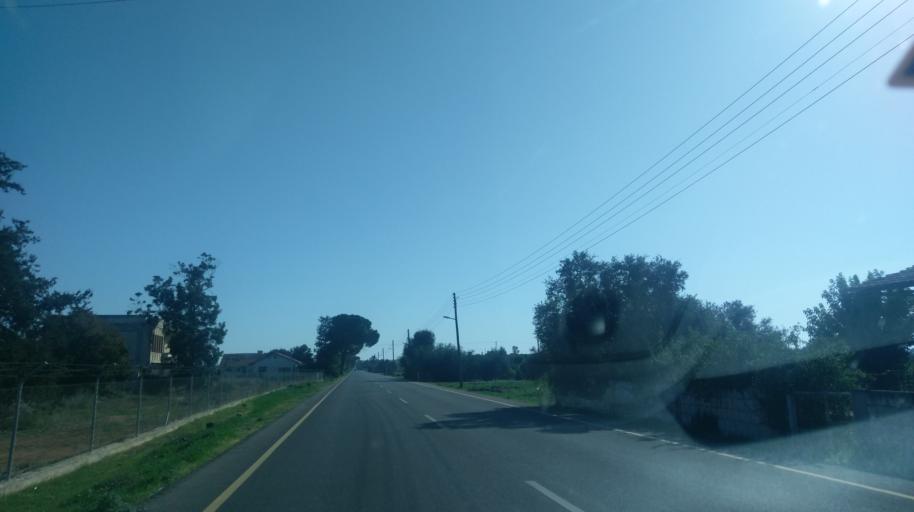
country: CY
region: Ammochostos
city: Famagusta
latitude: 35.0940
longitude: 33.9520
